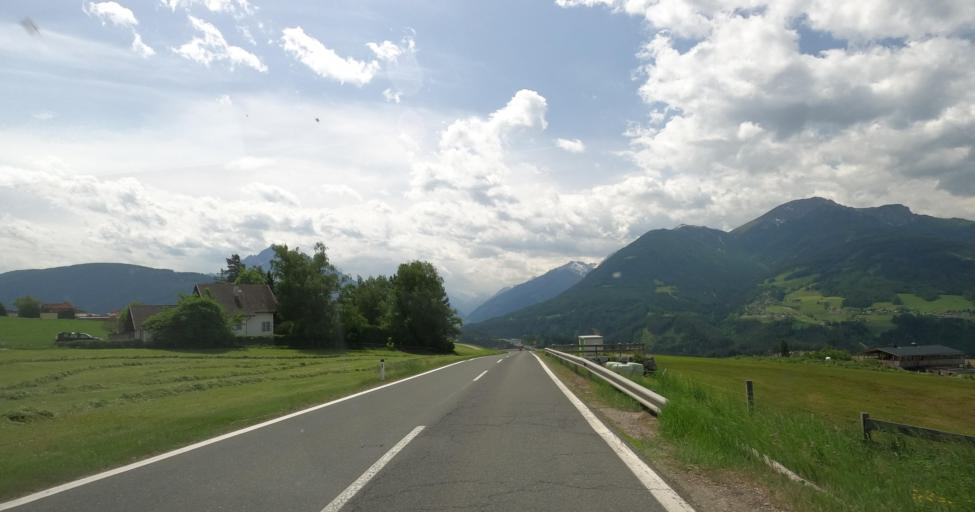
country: AT
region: Tyrol
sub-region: Politischer Bezirk Innsbruck Land
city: Patsch
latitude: 47.2101
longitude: 11.4156
